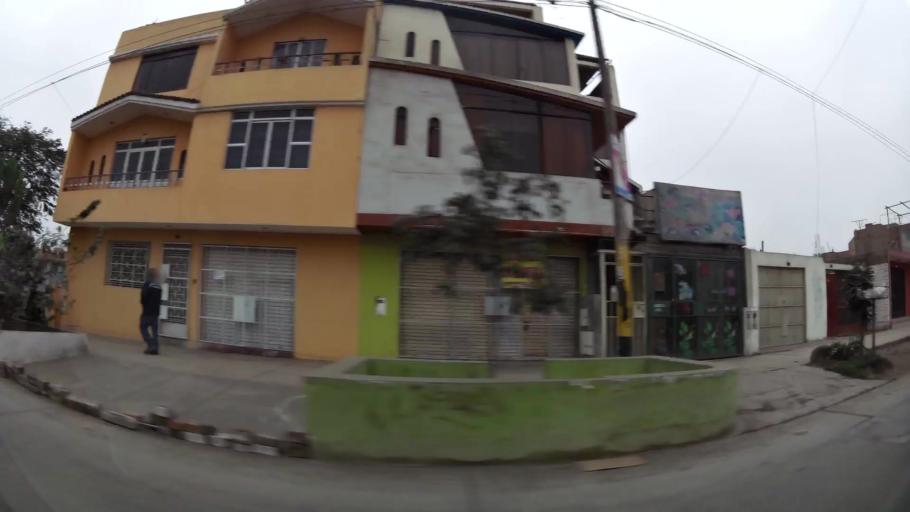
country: PE
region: Lima
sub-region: Lima
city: Urb. Santo Domingo
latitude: -11.8934
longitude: -77.0403
